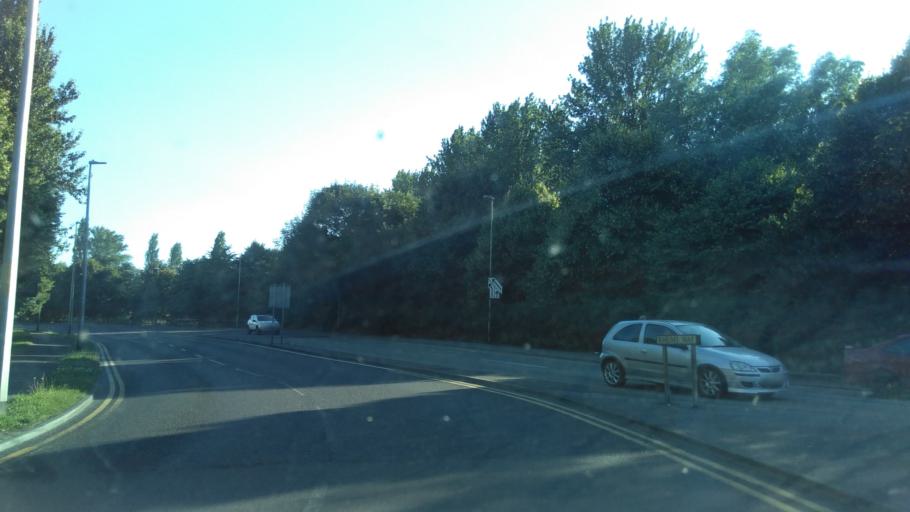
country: GB
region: England
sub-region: Kent
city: Canterbury
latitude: 51.2786
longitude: 1.0732
